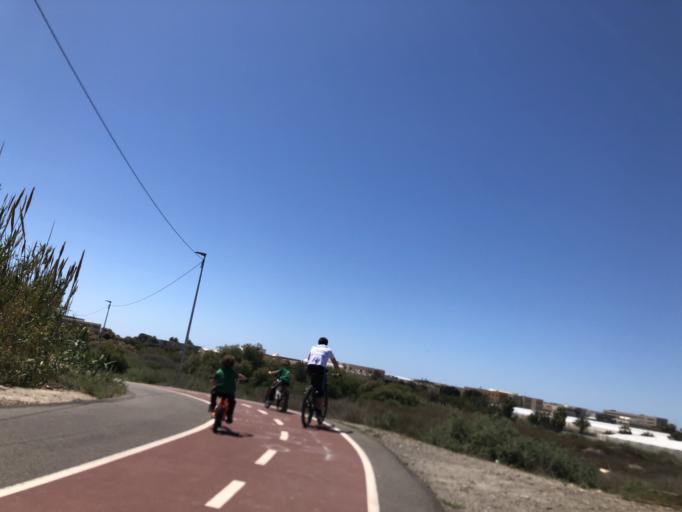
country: ES
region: Andalusia
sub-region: Provincia de Almeria
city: Almeria
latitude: 36.8350
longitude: -2.4035
